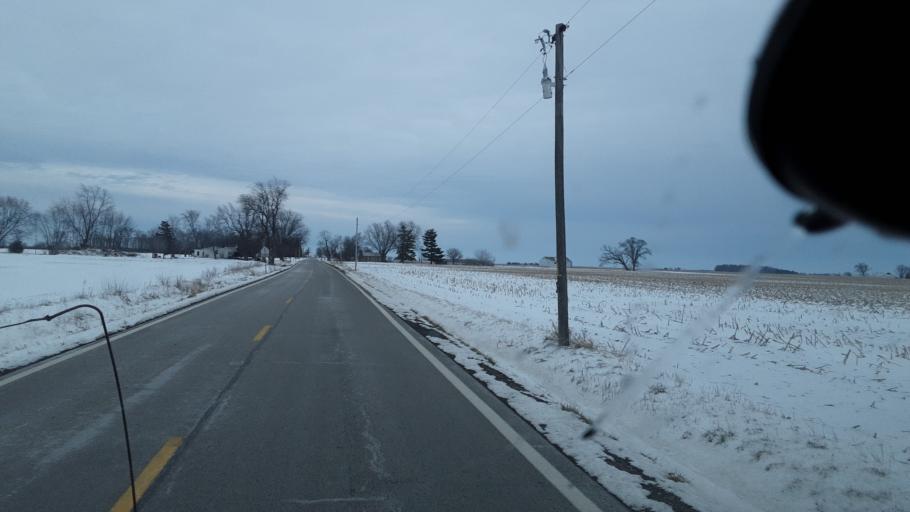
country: US
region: Ohio
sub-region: Pickaway County
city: Williamsport
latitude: 39.6545
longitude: -83.1174
